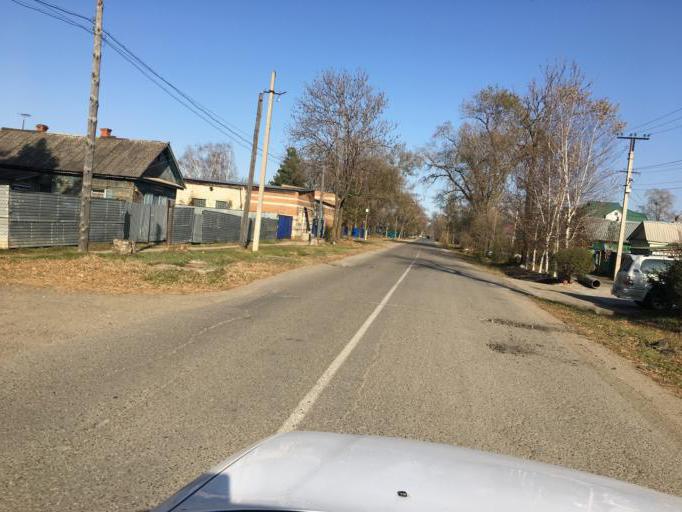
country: RU
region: Primorskiy
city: Dal'nerechensk
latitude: 45.9262
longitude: 133.7286
